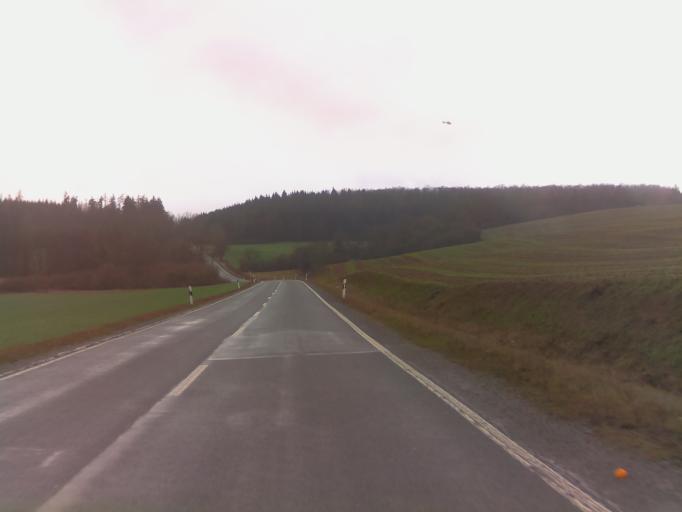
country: DE
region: Thuringia
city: Juchsen
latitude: 50.4740
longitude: 10.4904
